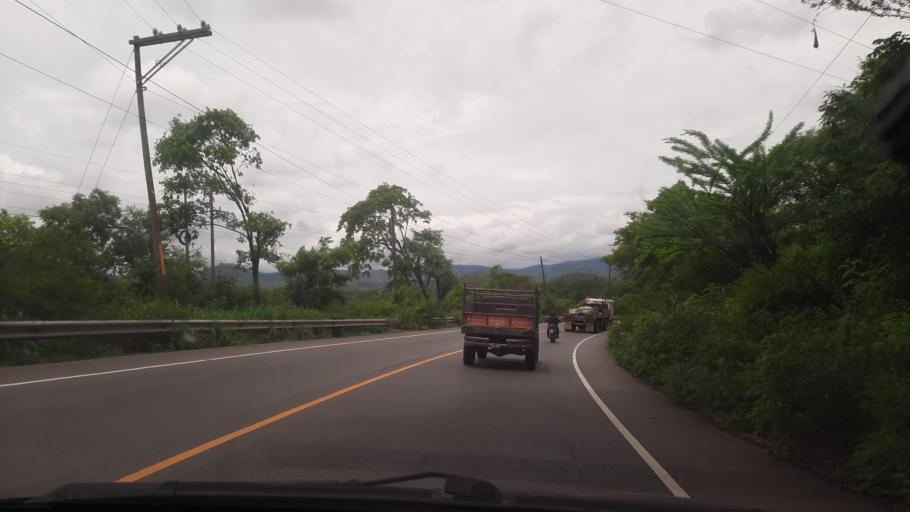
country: GT
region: Zacapa
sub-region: Municipio de Zacapa
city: Gualan
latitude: 15.1518
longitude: -89.3230
